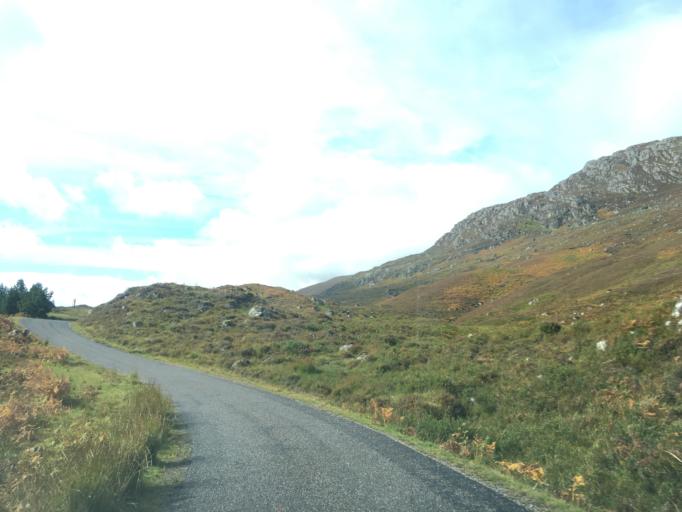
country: GB
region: Scotland
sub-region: Highland
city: Spean Bridge
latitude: 57.3412
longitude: -4.9508
